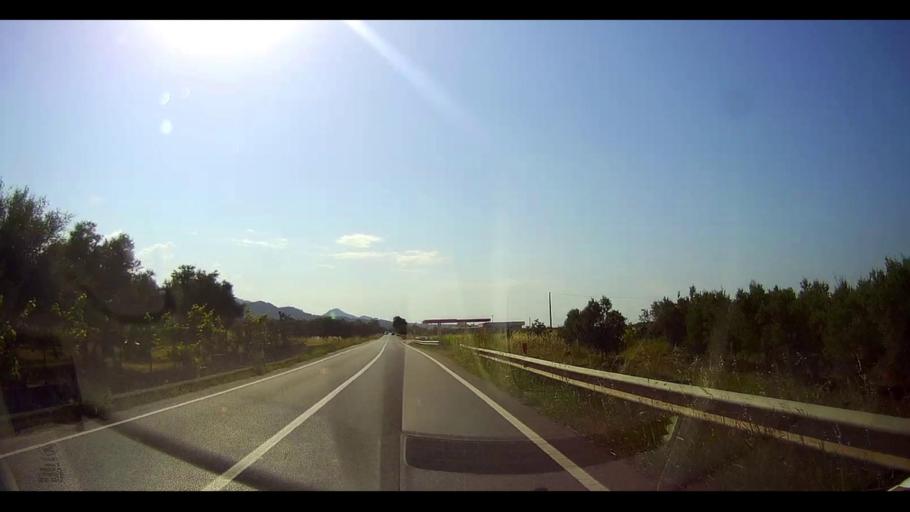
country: IT
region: Calabria
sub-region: Provincia di Cosenza
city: Cariati
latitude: 39.4787
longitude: 16.9964
